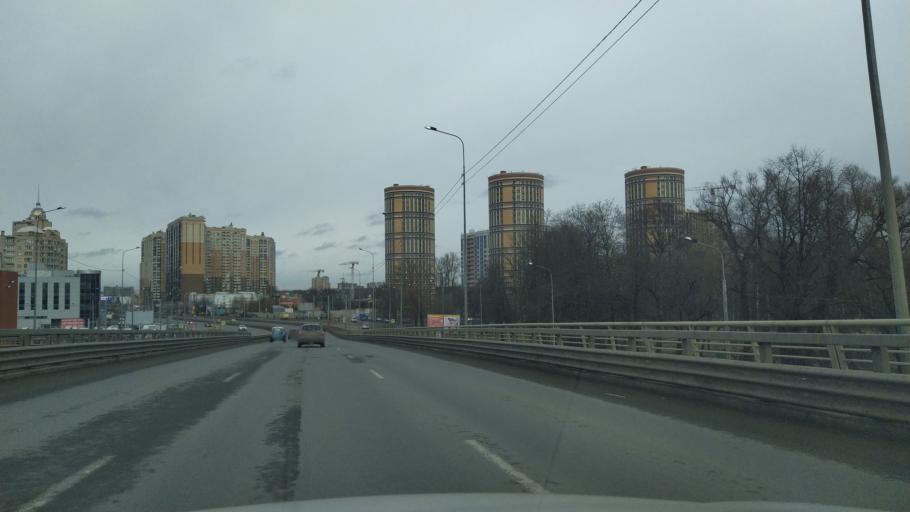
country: RU
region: Leningrad
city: Chernaya Rechka
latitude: 59.9941
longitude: 30.2997
